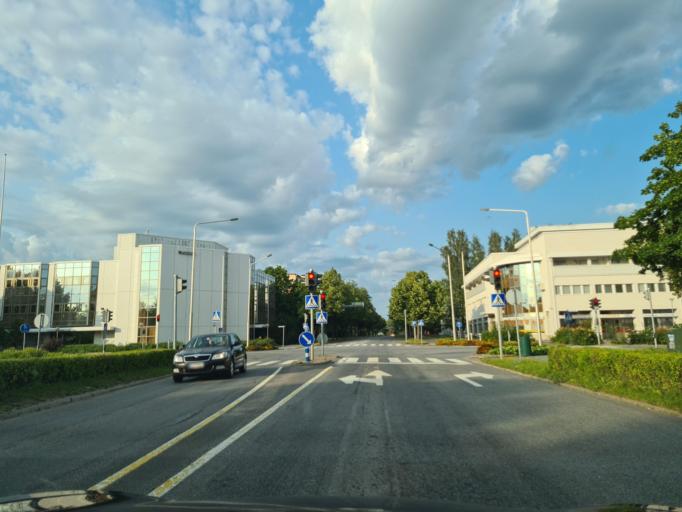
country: FI
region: Southern Ostrobothnia
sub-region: Seinaejoki
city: Lapua
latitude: 62.9717
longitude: 23.0015
